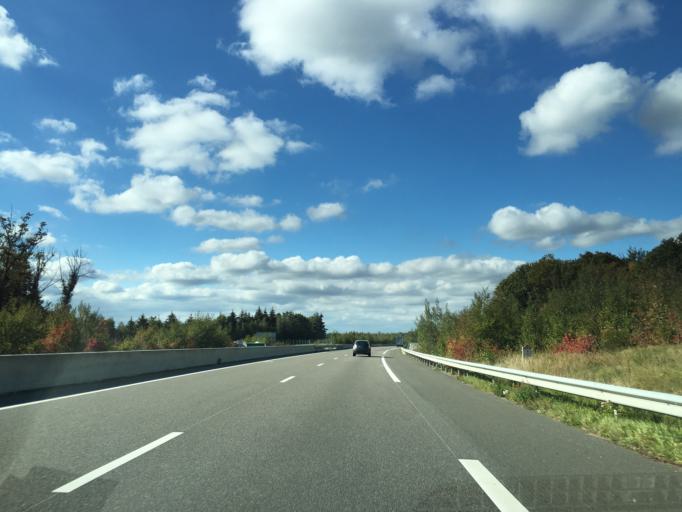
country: FR
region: Lorraine
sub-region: Departement de Meurthe-et-Moselle
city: Baccarat
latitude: 48.5041
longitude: 6.6781
